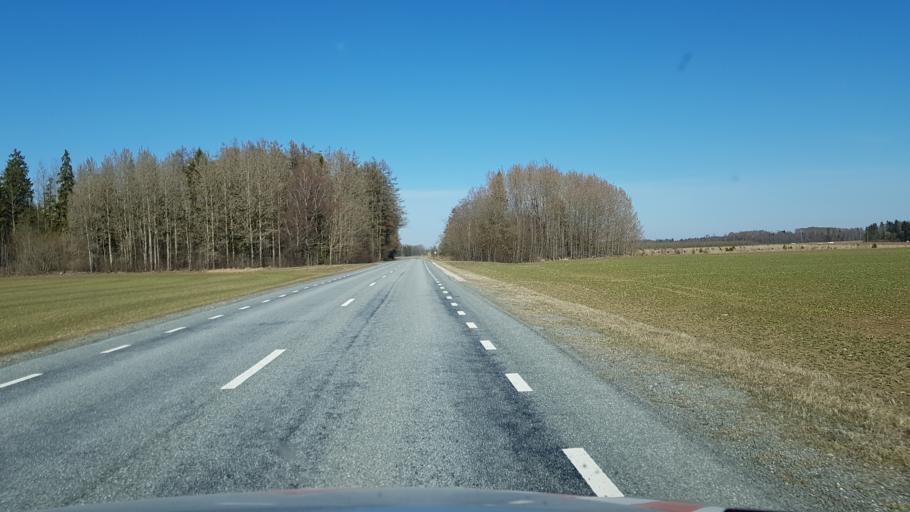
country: EE
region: Jaervamaa
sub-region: Jaerva-Jaani vald
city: Jarva-Jaani
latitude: 59.0867
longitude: 25.9723
